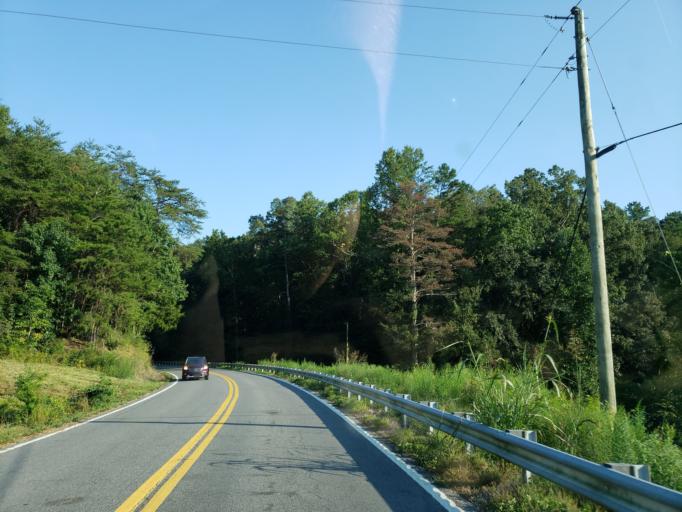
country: US
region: Tennessee
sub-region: Bradley County
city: Wildwood Lake
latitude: 35.0046
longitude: -84.7841
